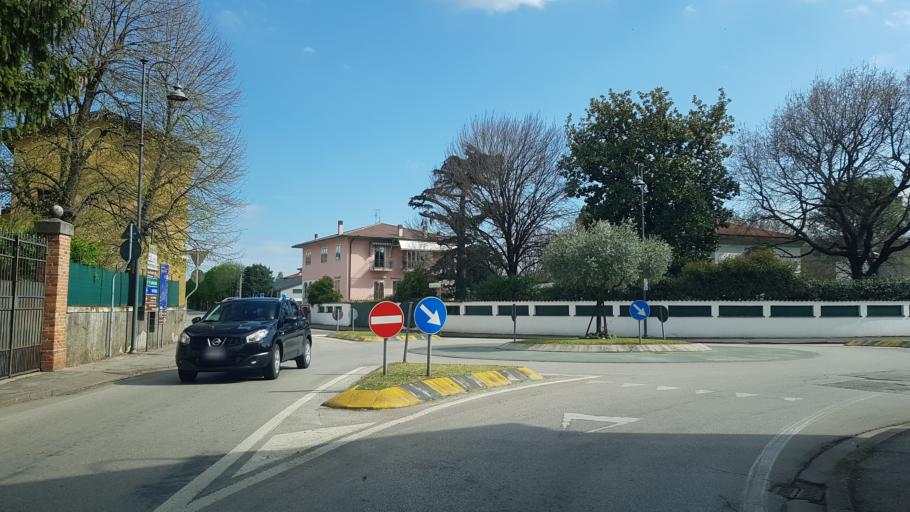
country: IT
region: Veneto
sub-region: Provincia di Vicenza
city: Lonigo
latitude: 45.3883
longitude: 11.3930
